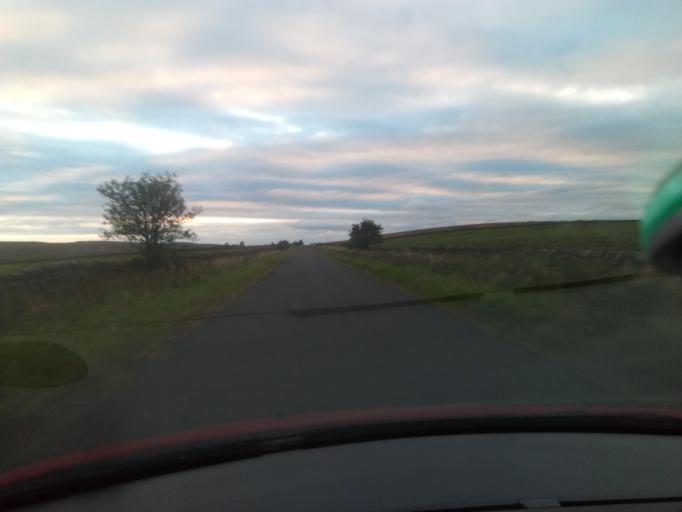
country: GB
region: England
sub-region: Northumberland
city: Bardon Mill
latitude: 54.9287
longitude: -2.3591
